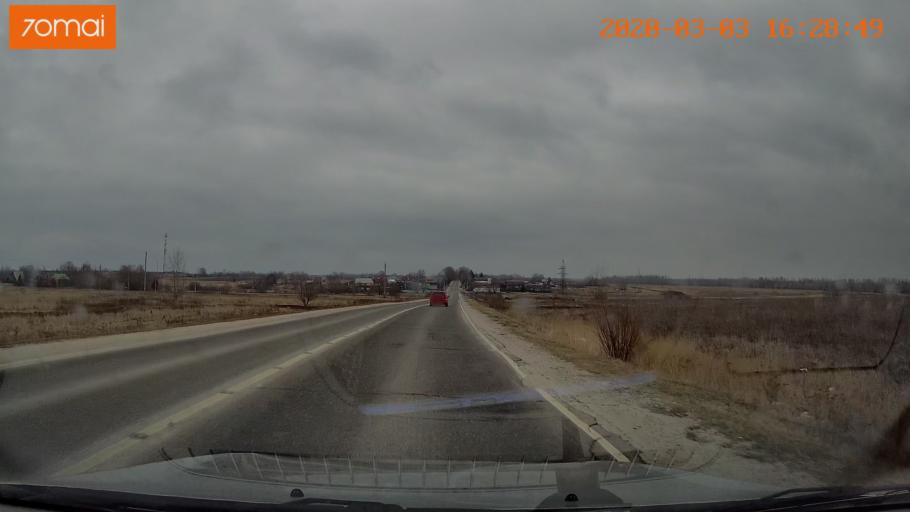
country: RU
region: Moskovskaya
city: Konobeyevo
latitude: 55.4386
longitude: 38.6934
